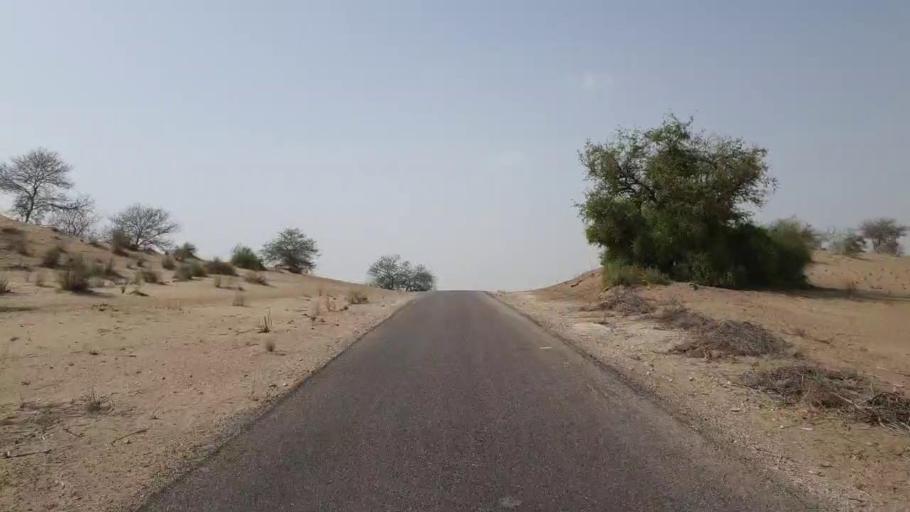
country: PK
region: Sindh
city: Mithi
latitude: 24.5882
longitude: 69.9227
